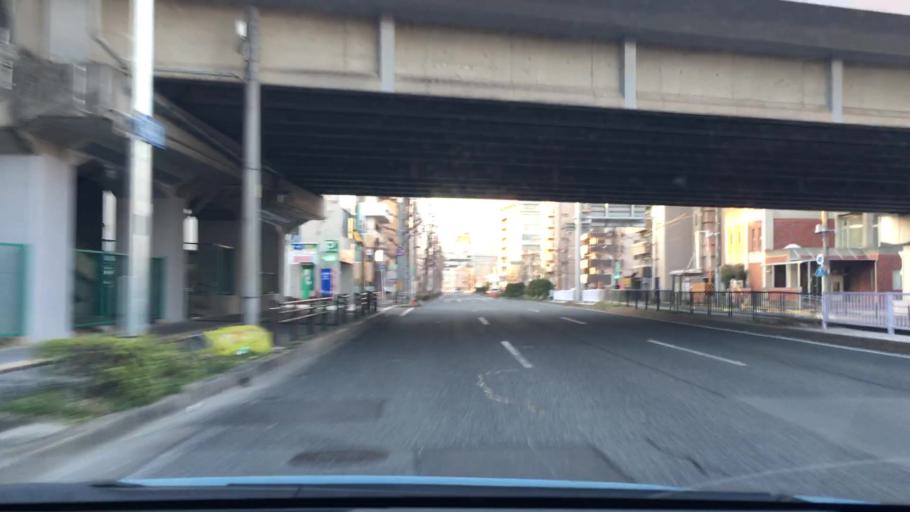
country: JP
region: Aichi
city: Nagoya-shi
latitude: 35.1298
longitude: 136.9091
